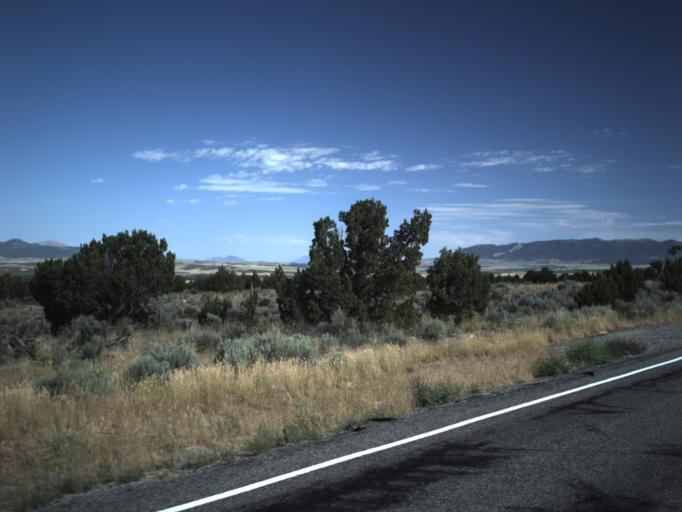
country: US
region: Utah
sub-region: Juab County
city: Mona
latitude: 39.8210
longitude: -112.1412
